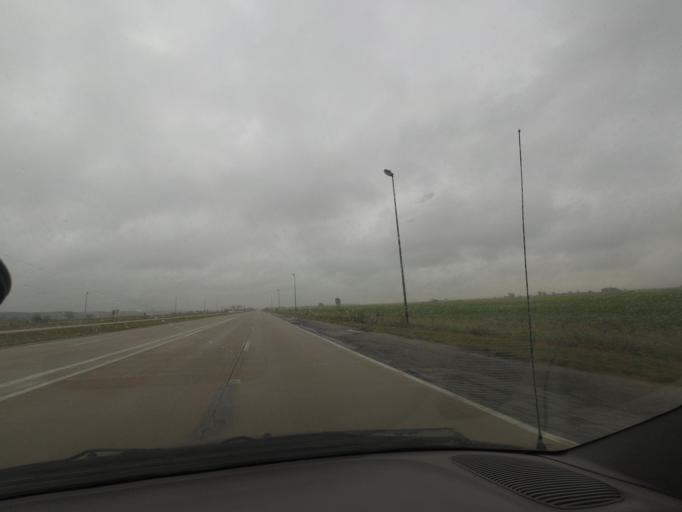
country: US
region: Missouri
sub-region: Marion County
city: Hannibal
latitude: 39.7516
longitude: -91.2914
